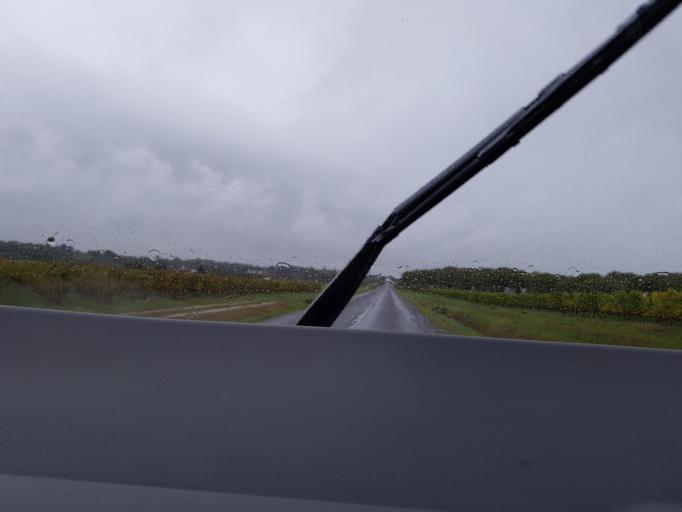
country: FR
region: Aquitaine
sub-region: Departement de la Gironde
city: Reignac
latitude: 45.2367
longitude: -0.5175
